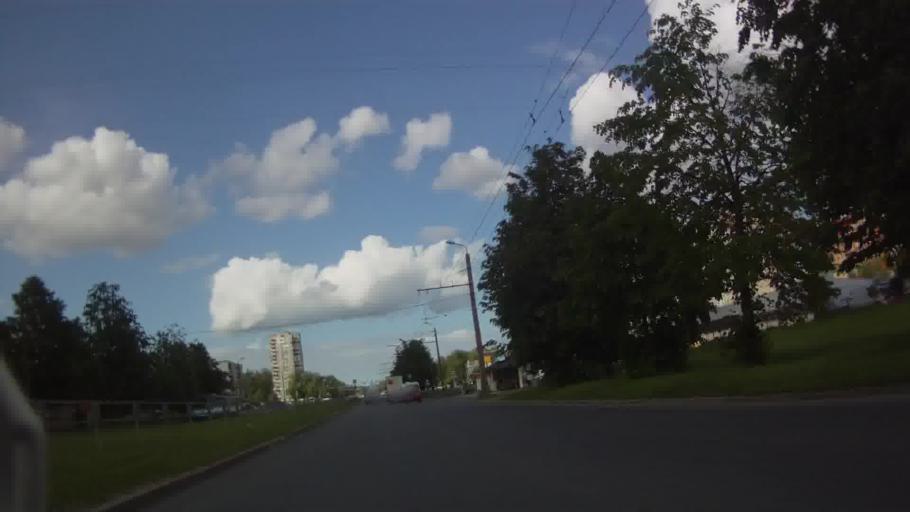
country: LV
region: Stopini
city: Ulbroka
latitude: 56.9365
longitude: 24.2029
